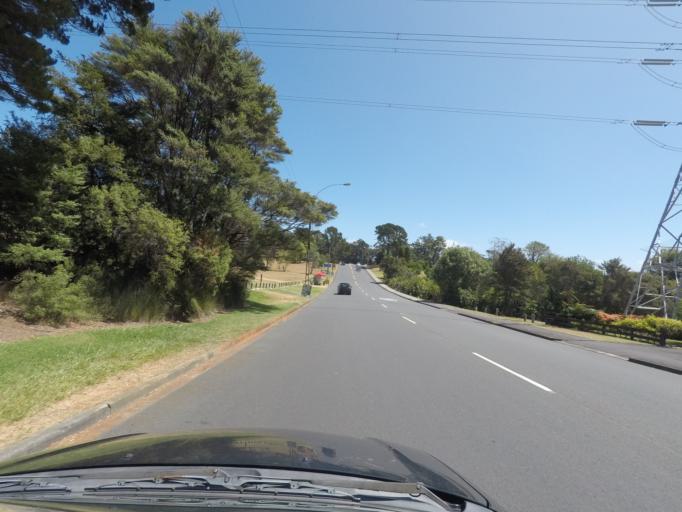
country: NZ
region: Auckland
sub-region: Auckland
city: Waitakere
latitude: -36.9262
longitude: 174.6915
